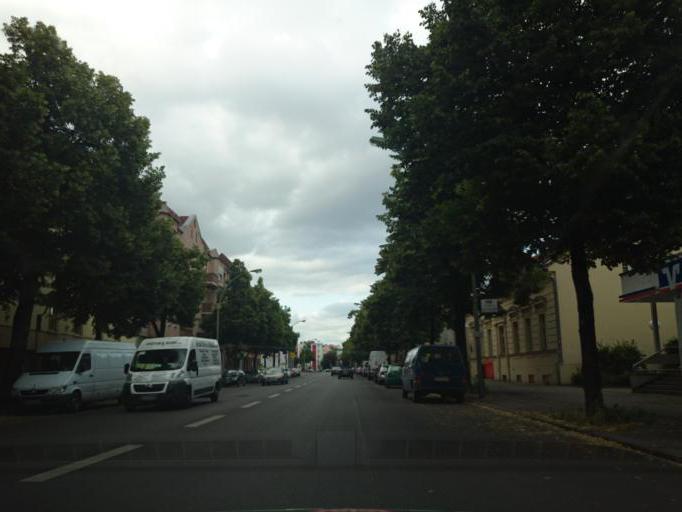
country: DE
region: Berlin
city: Britz
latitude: 52.4503
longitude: 13.4373
